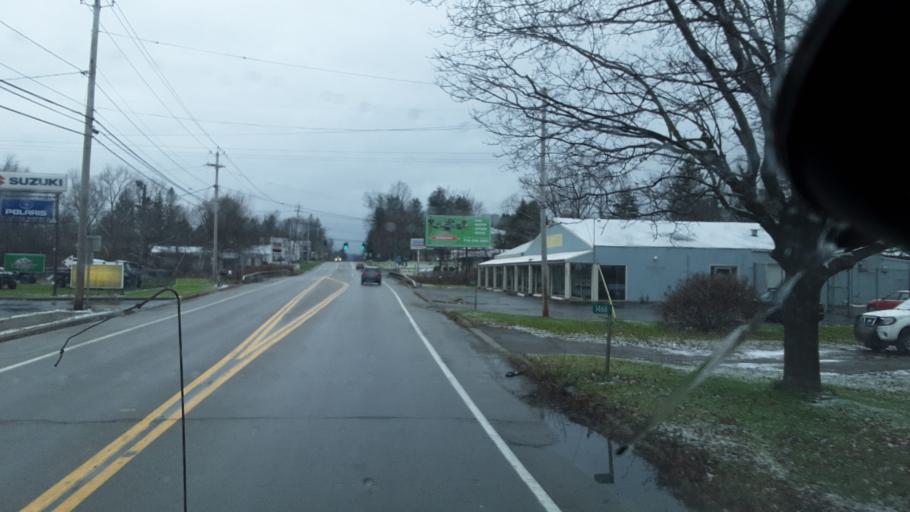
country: US
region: New York
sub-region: Cattaraugus County
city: Westons Mills
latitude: 42.0660
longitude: -78.3835
